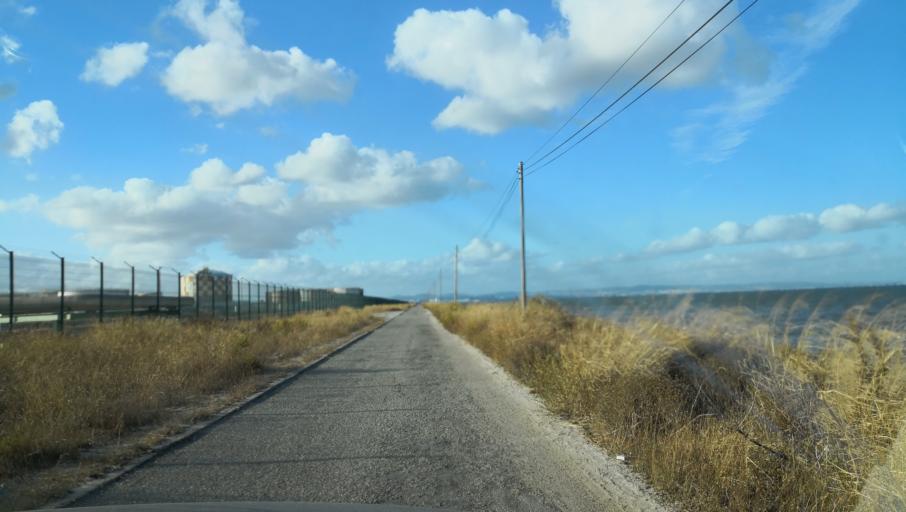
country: PT
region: Setubal
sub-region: Barreiro
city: Barreiro
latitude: 38.6777
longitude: -9.0546
